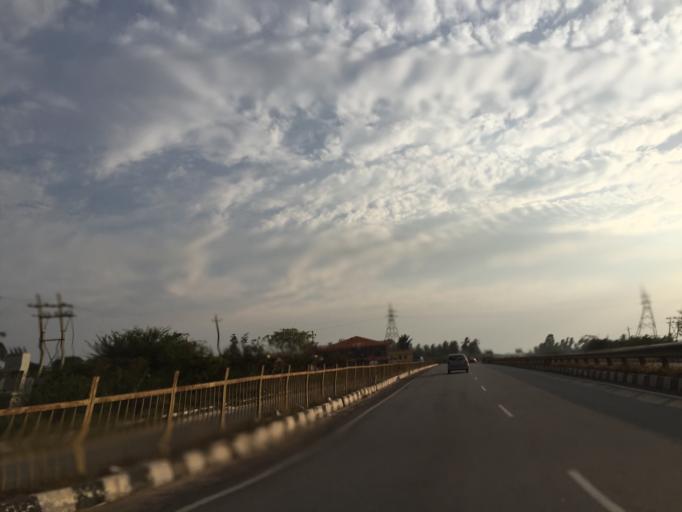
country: IN
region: Karnataka
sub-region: Kolar
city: Kolar
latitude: 13.1275
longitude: 78.1561
